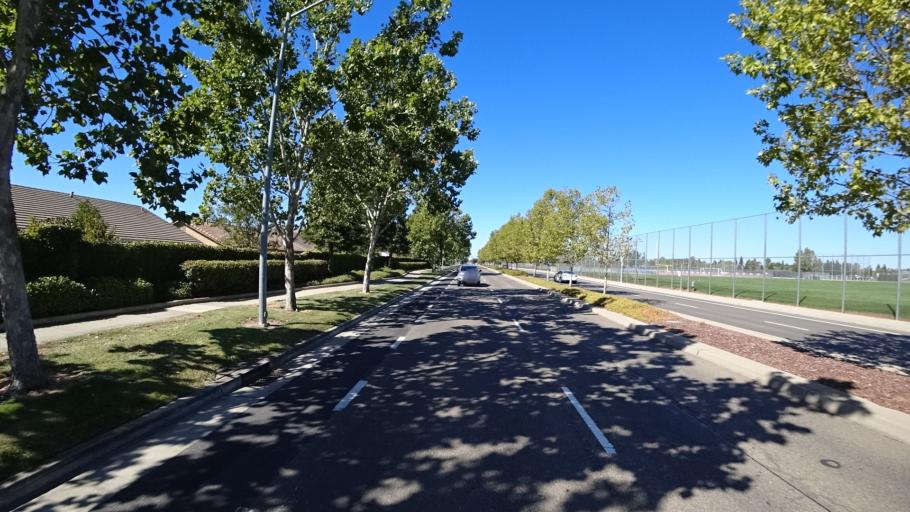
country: US
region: California
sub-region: Sacramento County
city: Elk Grove
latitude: 38.4236
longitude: -121.3399
